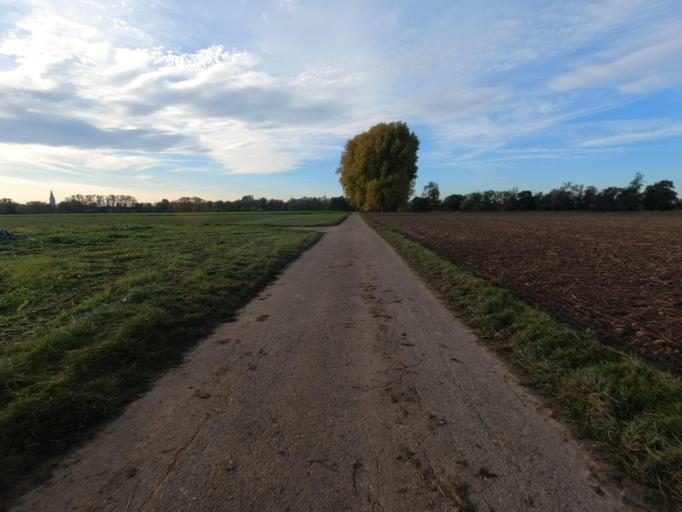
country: DE
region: North Rhine-Westphalia
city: Huckelhoven
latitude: 51.0446
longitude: 6.2156
